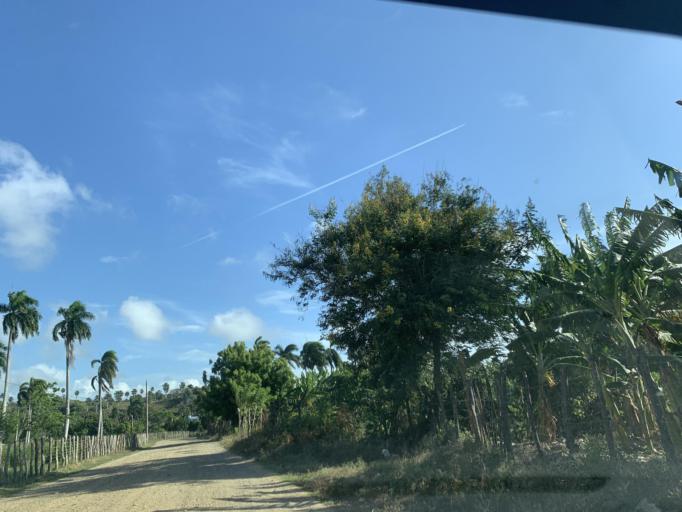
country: DO
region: Puerto Plata
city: Luperon
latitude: 19.8925
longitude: -70.8841
